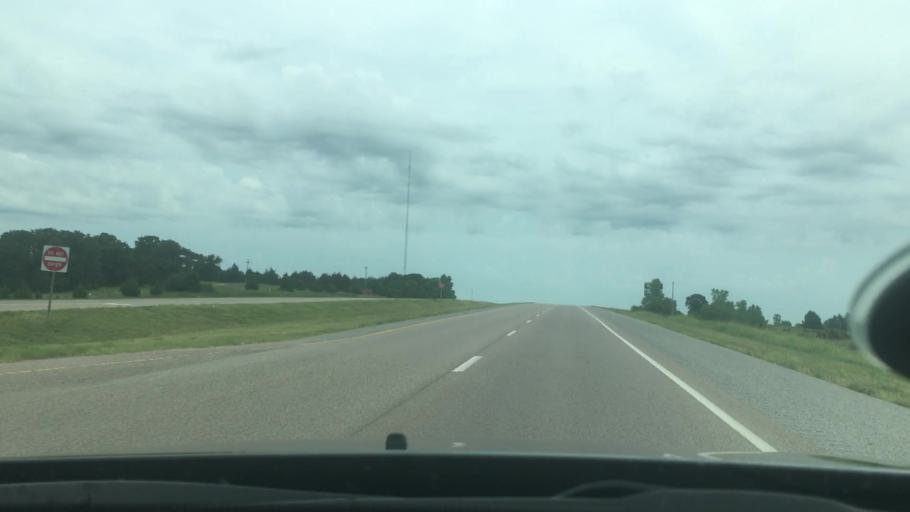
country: US
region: Oklahoma
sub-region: Pontotoc County
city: Byng
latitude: 34.8903
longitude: -96.6750
